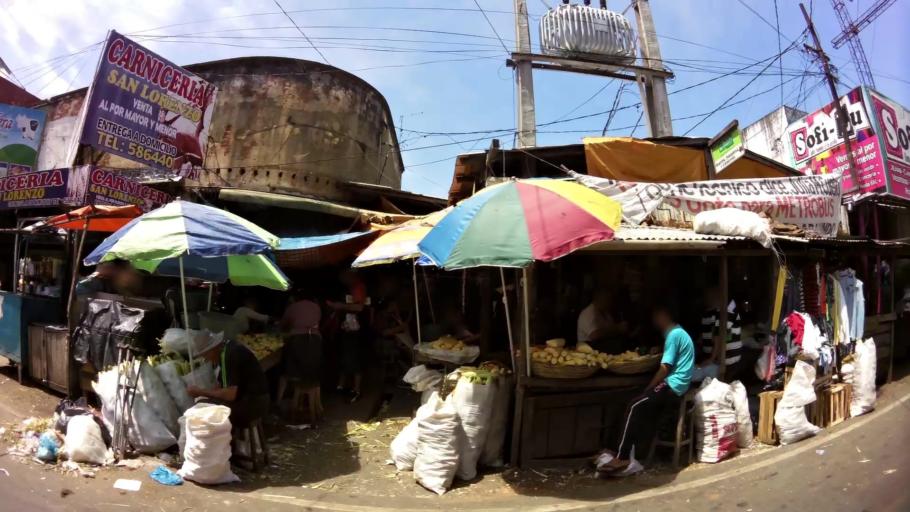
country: PY
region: Central
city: San Lorenzo
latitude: -25.3452
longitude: -57.5112
